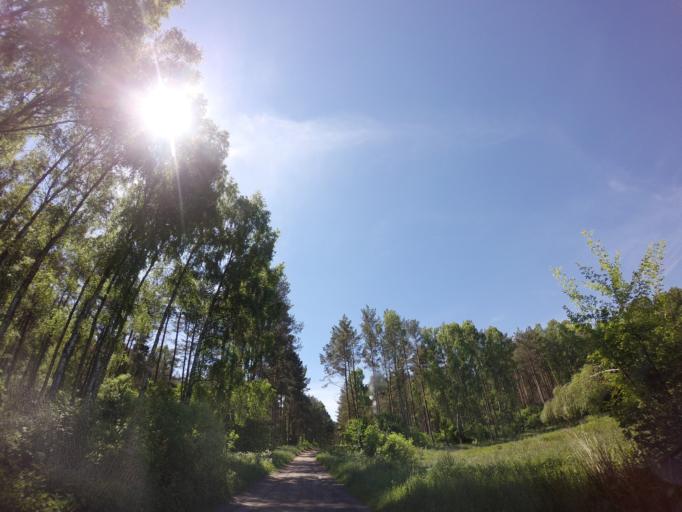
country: PL
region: West Pomeranian Voivodeship
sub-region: Powiat choszczenski
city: Drawno
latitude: 53.2949
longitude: 15.6904
